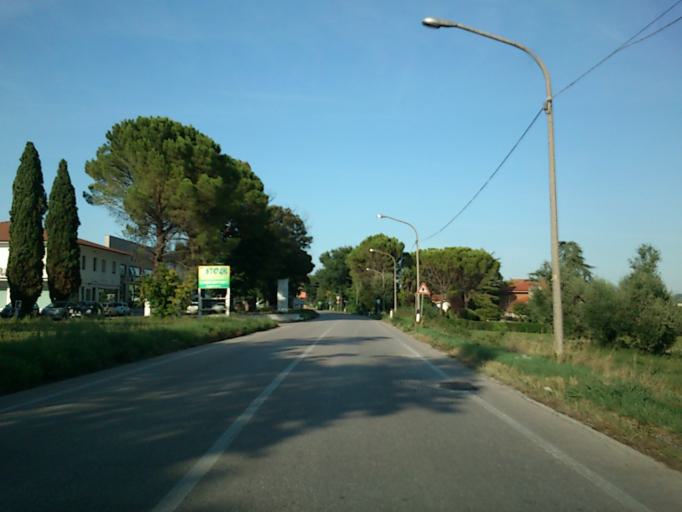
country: IT
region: The Marches
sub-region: Provincia di Pesaro e Urbino
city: Fossombrone
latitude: 43.7003
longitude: 12.8308
